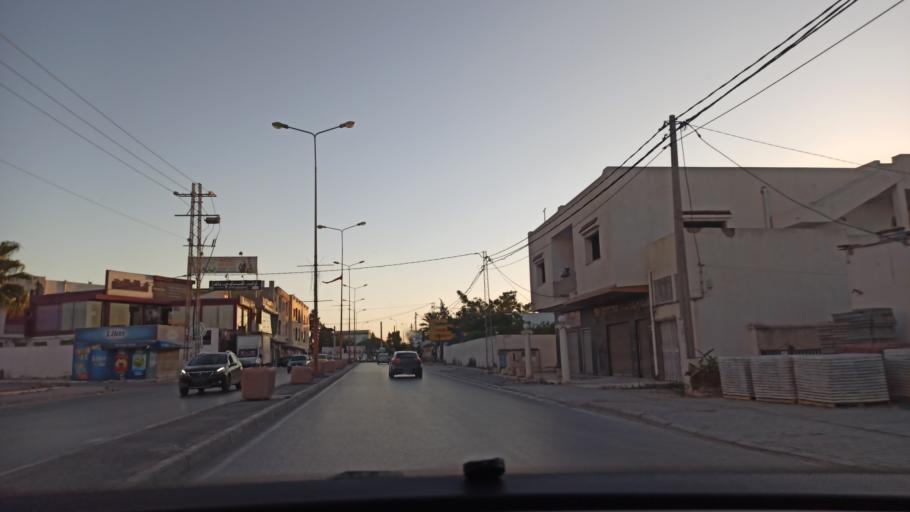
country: TN
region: Ariana
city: Ariana
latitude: 36.8605
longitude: 10.2080
